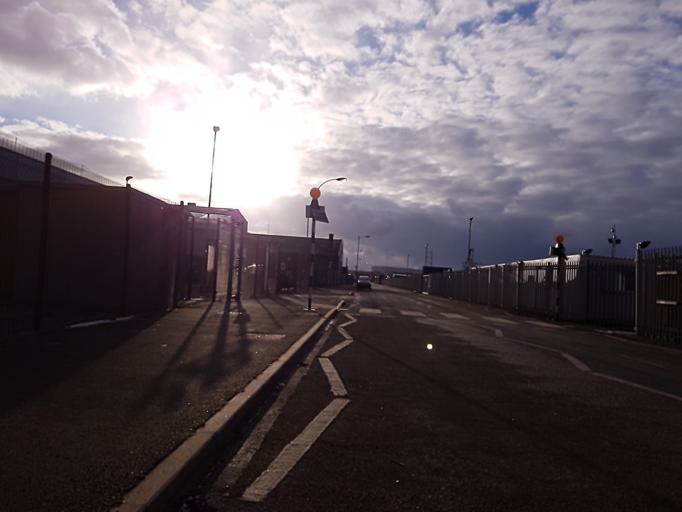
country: GB
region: England
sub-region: North East Lincolnshire
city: Grimsby
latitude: 53.5813
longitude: -0.0618
